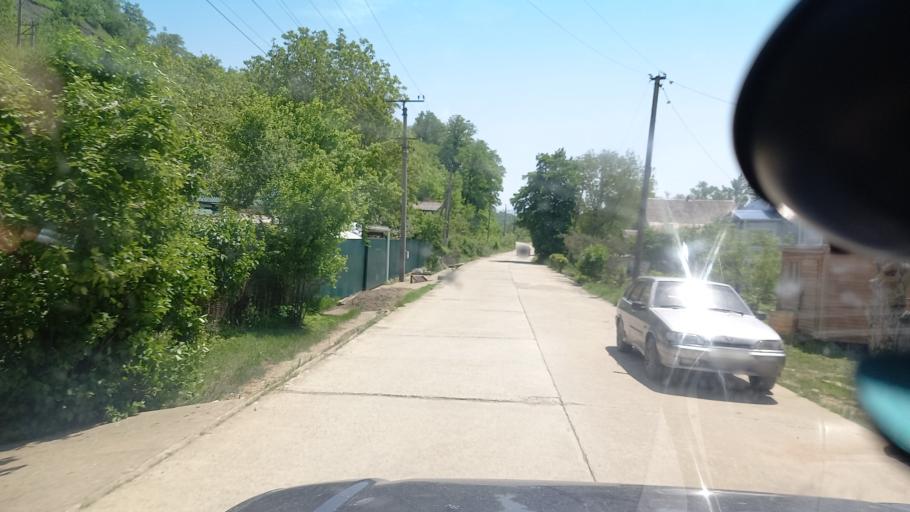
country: RU
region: Krasnodarskiy
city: Tuapse
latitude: 44.2436
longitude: 39.2400
